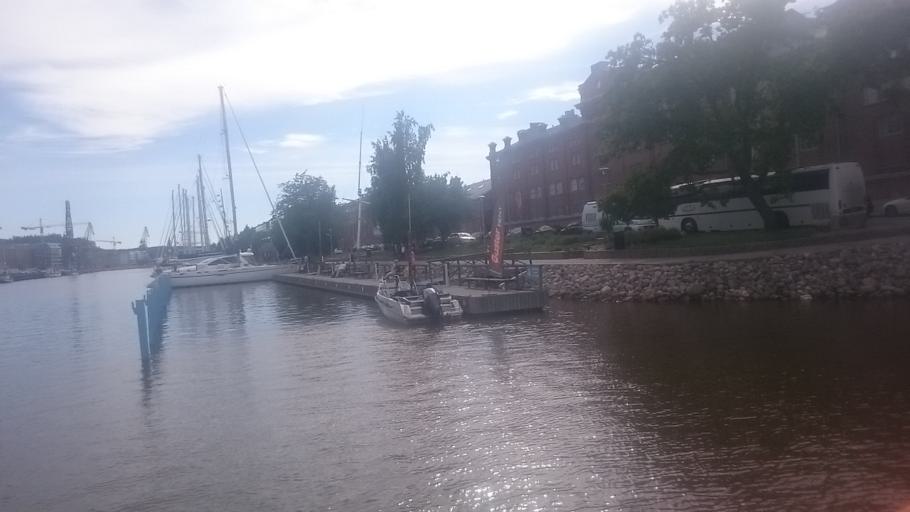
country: FI
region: Varsinais-Suomi
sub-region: Turku
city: Turku
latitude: 60.4412
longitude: 22.2476
